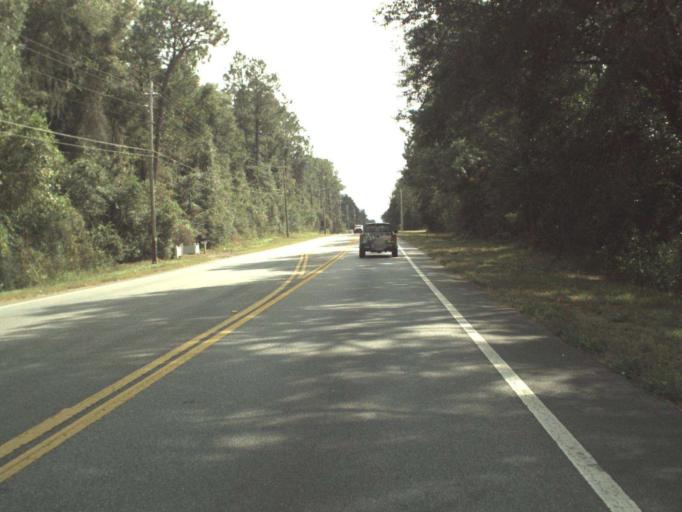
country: US
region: Florida
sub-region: Leon County
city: Woodville
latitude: 30.3597
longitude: -84.2632
